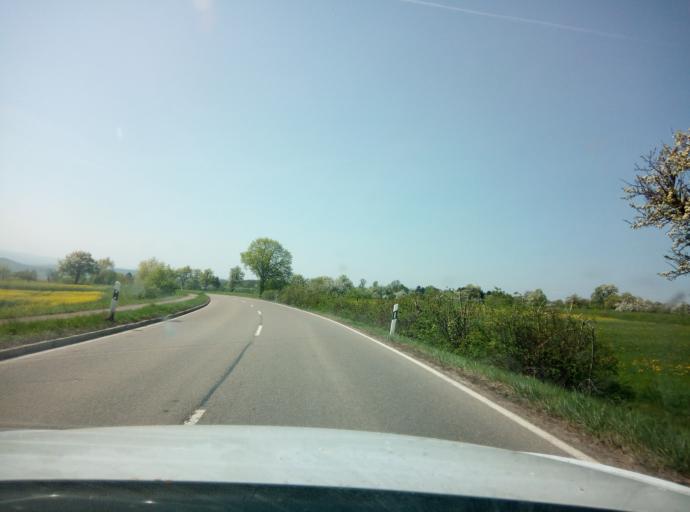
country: DE
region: Baden-Wuerttemberg
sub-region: Tuebingen Region
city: Kusterdingen
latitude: 48.5444
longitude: 9.0953
